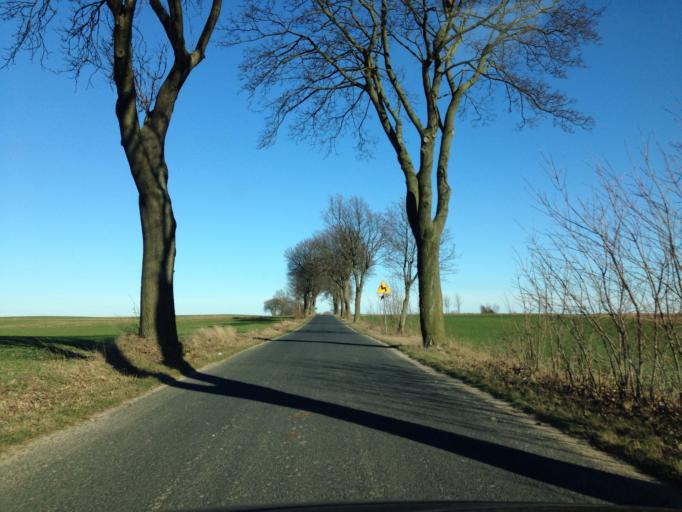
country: PL
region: Kujawsko-Pomorskie
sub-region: Powiat brodnicki
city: Brzozie
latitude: 53.3618
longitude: 19.6319
